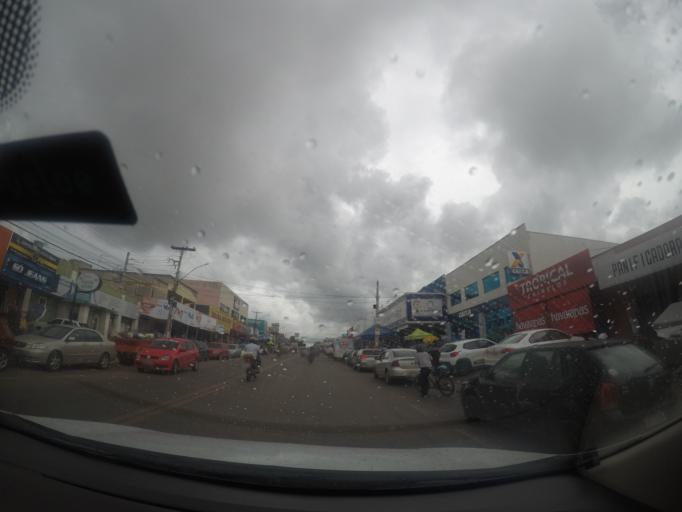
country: BR
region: Goias
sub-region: Trindade
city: Trindade
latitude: -16.6417
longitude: -49.3903
